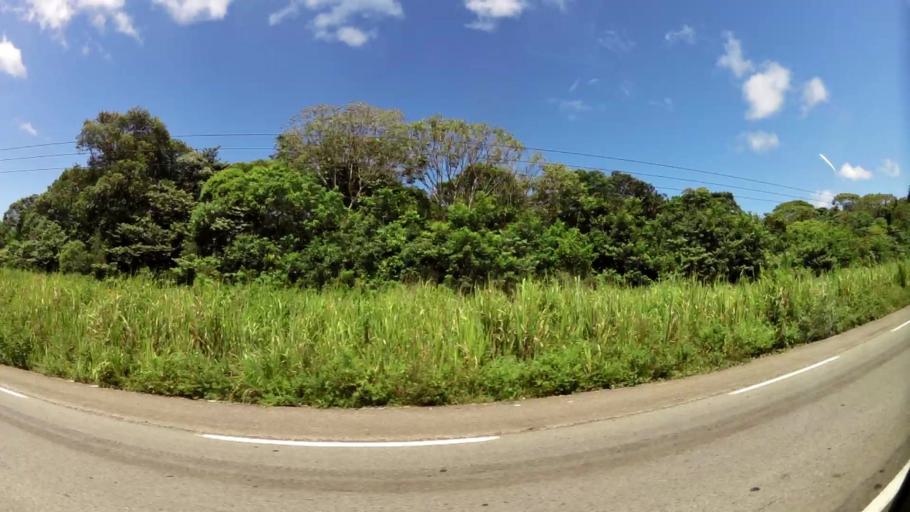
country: GF
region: Guyane
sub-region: Guyane
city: Matoury
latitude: 4.8656
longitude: -52.3338
